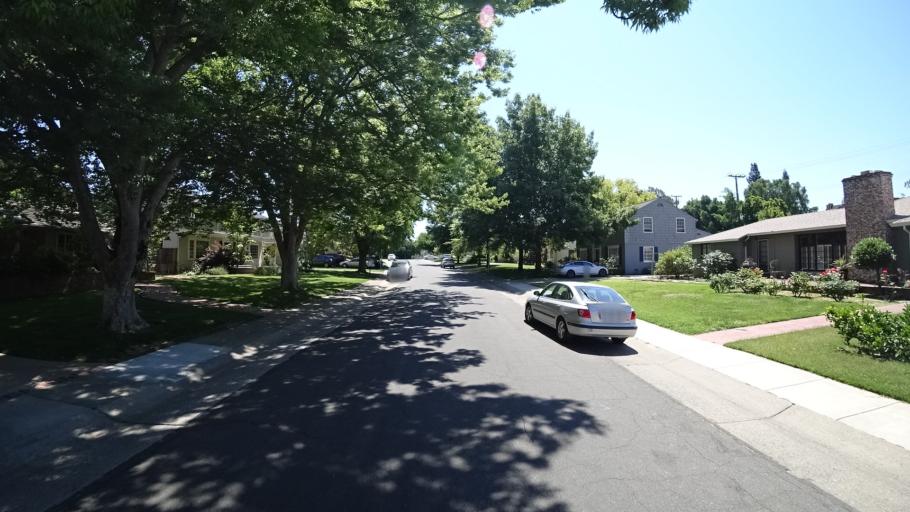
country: US
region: California
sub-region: Sacramento County
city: Sacramento
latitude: 38.5464
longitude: -121.4921
